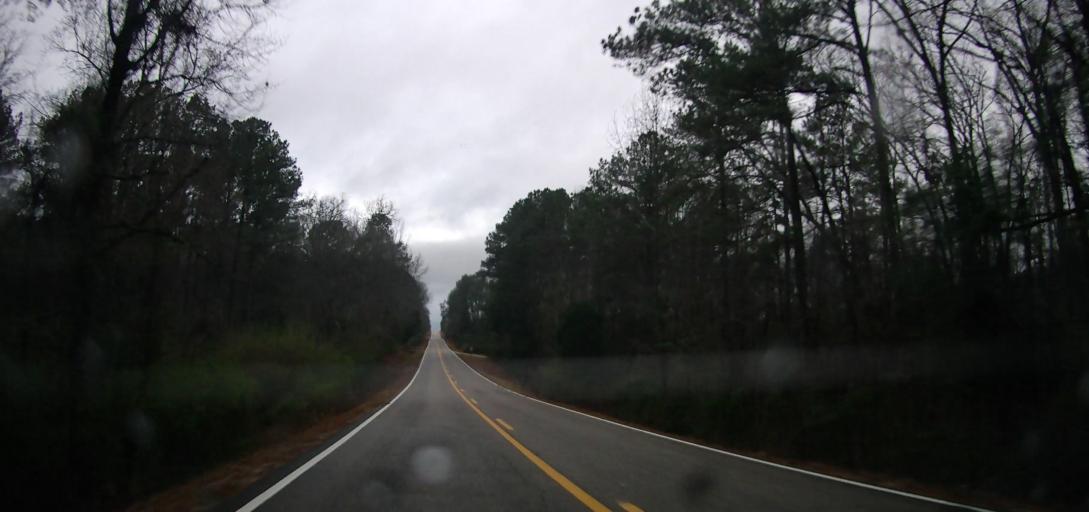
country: US
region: Alabama
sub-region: Bibb County
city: Centreville
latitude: 33.0248
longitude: -87.1441
